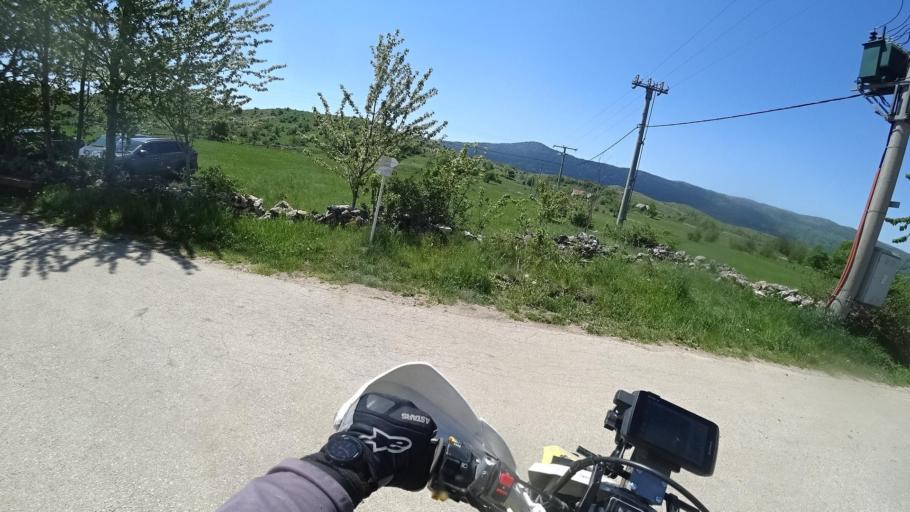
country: BA
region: Federation of Bosnia and Herzegovina
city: Rumboci
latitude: 43.8311
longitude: 17.4499
